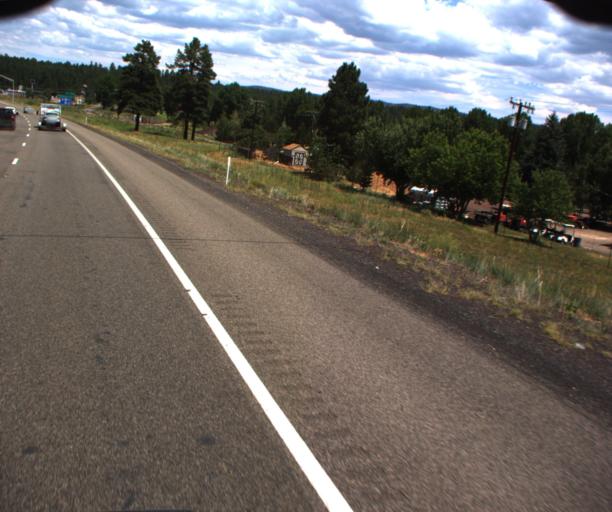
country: US
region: Arizona
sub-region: Coconino County
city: Sedona
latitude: 34.9355
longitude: -111.6492
